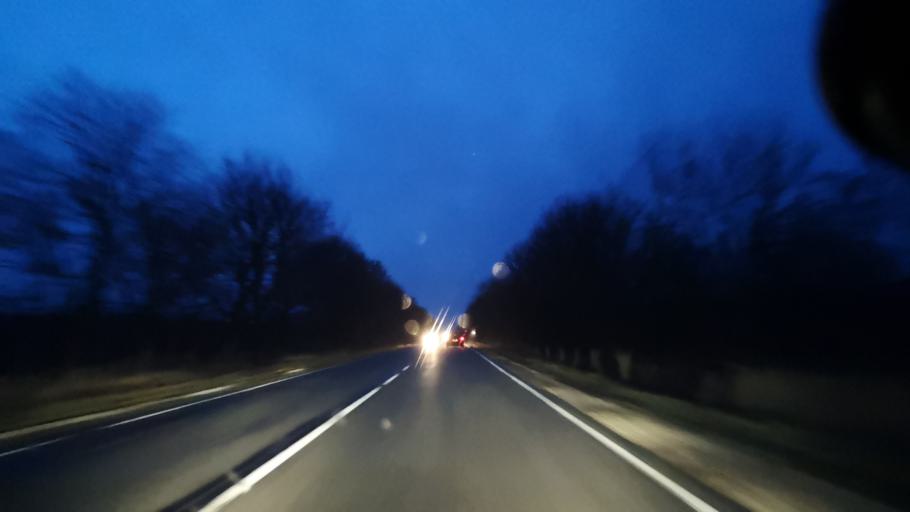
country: MD
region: Orhei
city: Orhei
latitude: 47.4659
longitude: 28.7912
